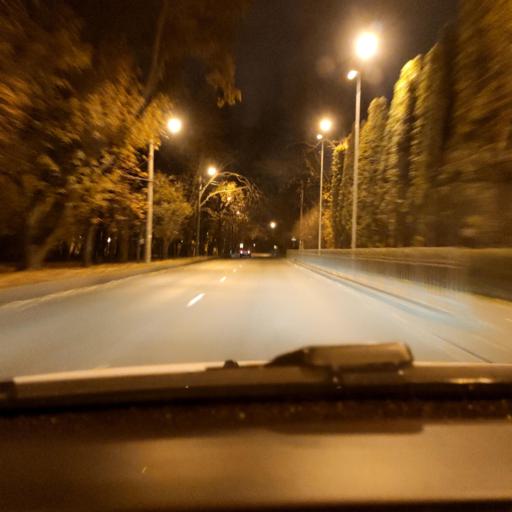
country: RU
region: Voronezj
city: Voronezh
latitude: 51.7107
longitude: 39.2259
